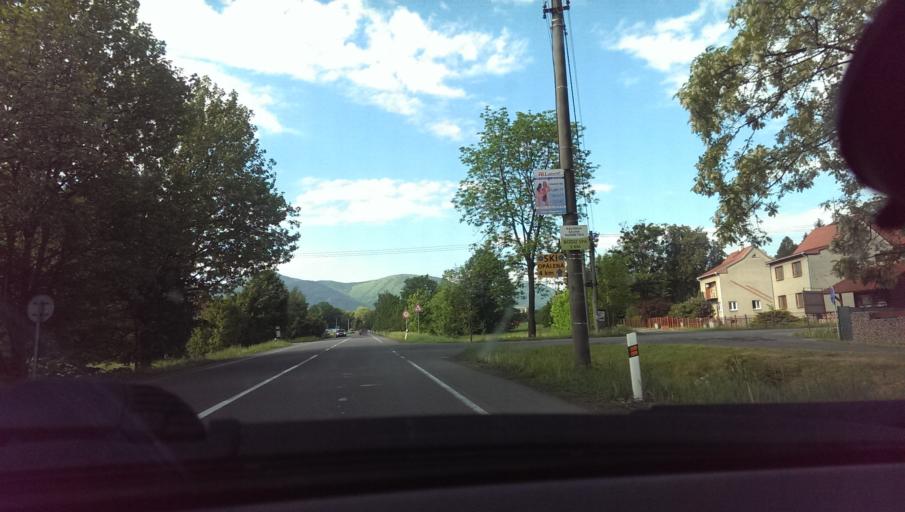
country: CZ
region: Moravskoslezsky
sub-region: Okres Frydek-Mistek
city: Celadna
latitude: 49.5646
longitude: 18.3527
